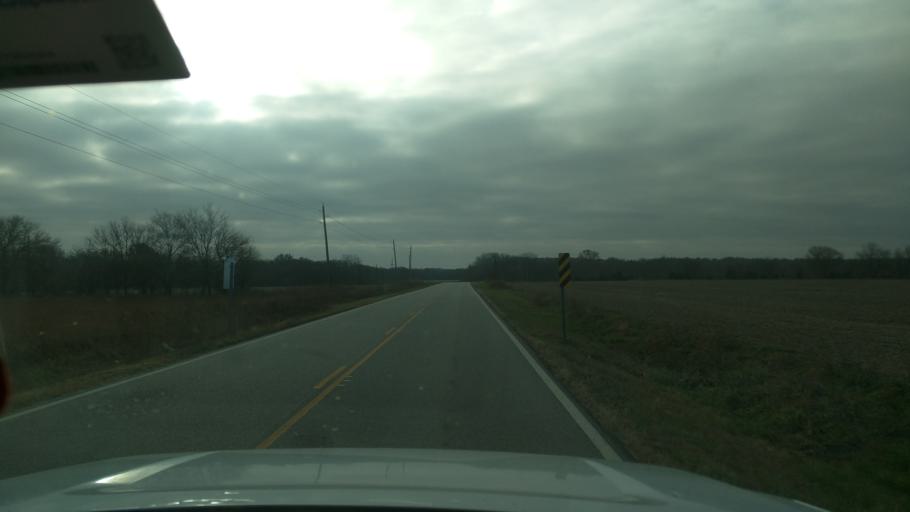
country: US
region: Kansas
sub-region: Greenwood County
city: Eureka
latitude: 37.7139
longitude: -96.2279
